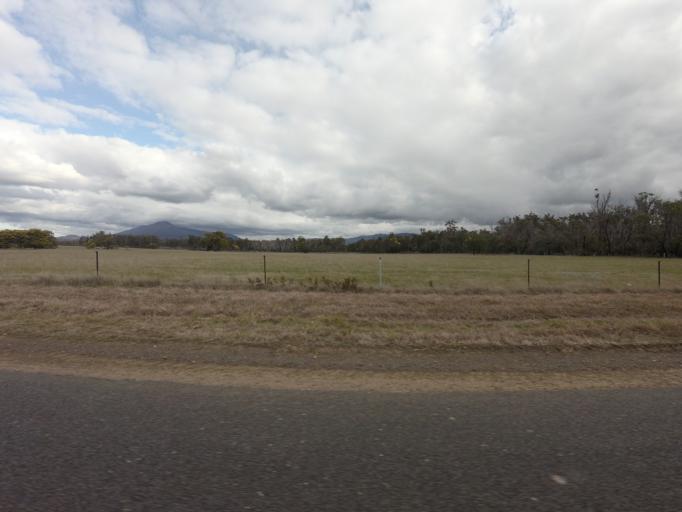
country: AU
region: Tasmania
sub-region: Northern Midlands
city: Longford
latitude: -41.8029
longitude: 147.1422
